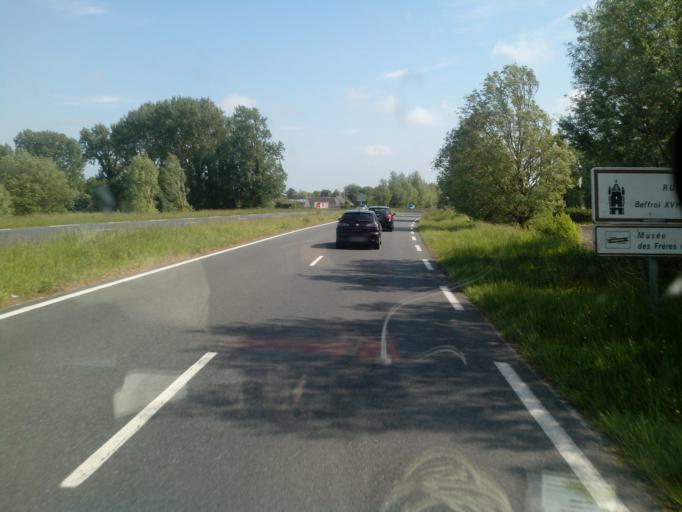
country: FR
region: Picardie
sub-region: Departement de la Somme
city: Rue
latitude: 50.2798
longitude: 1.6589
